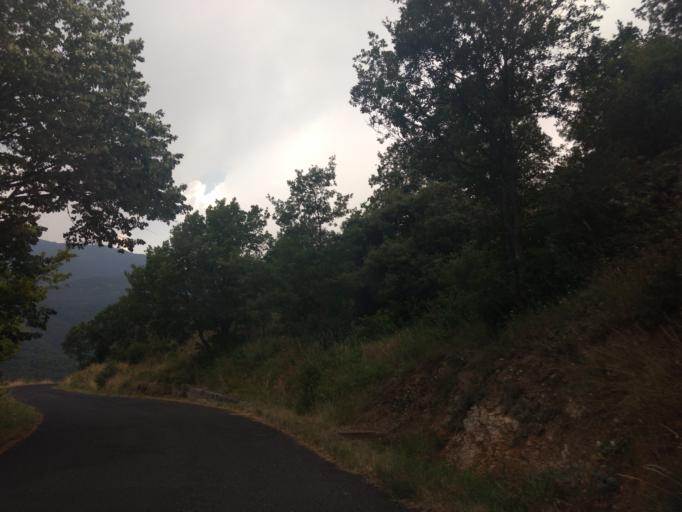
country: FR
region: Languedoc-Roussillon
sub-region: Departement des Pyrenees-Orientales
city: Vernet-les-Bains
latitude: 42.5670
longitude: 2.2991
